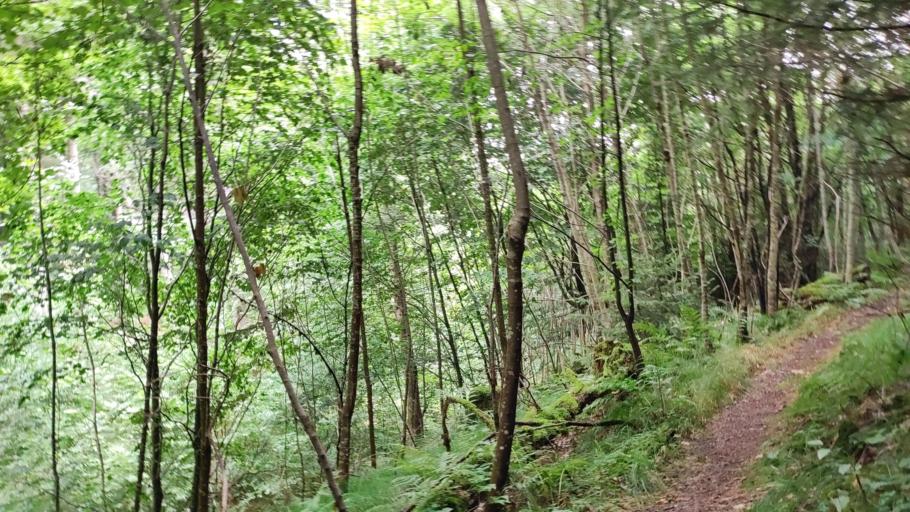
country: DE
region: Bavaria
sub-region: Swabia
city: Jettingen-Scheppach
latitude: 48.3791
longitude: 10.4019
